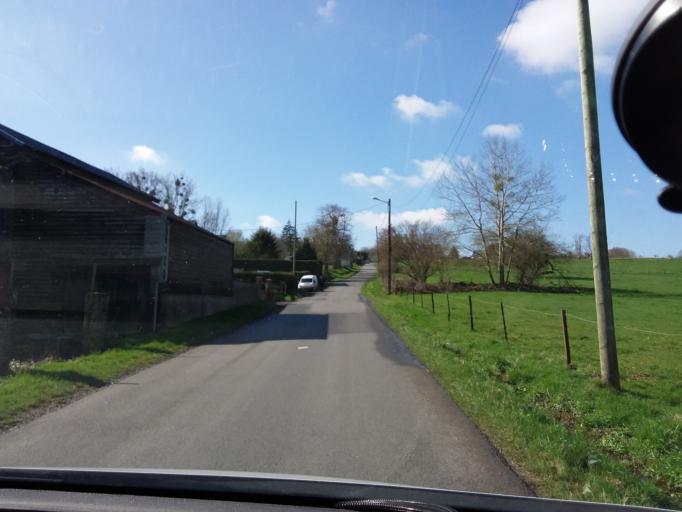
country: FR
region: Picardie
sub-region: Departement de l'Aisne
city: Hirson
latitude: 49.8489
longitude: 4.0782
